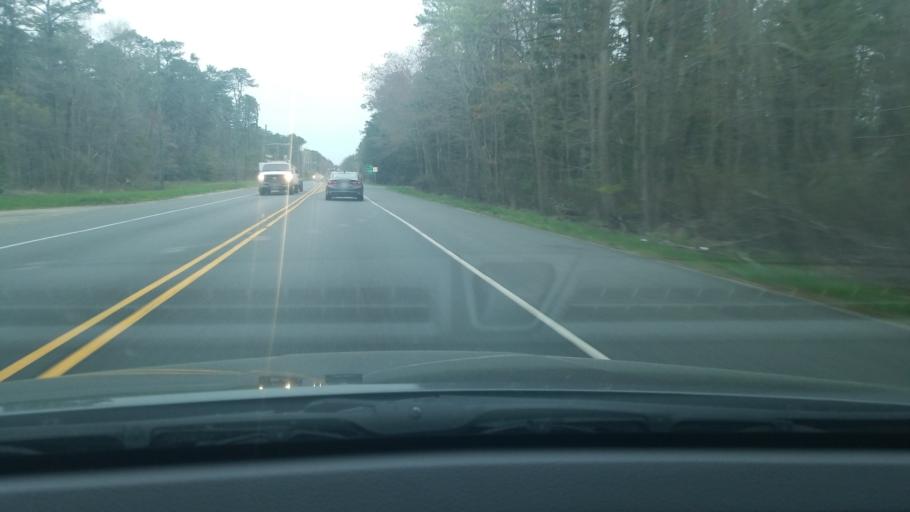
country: US
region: New Jersey
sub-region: Burlington County
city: Leisuretowne
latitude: 39.8859
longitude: -74.7124
